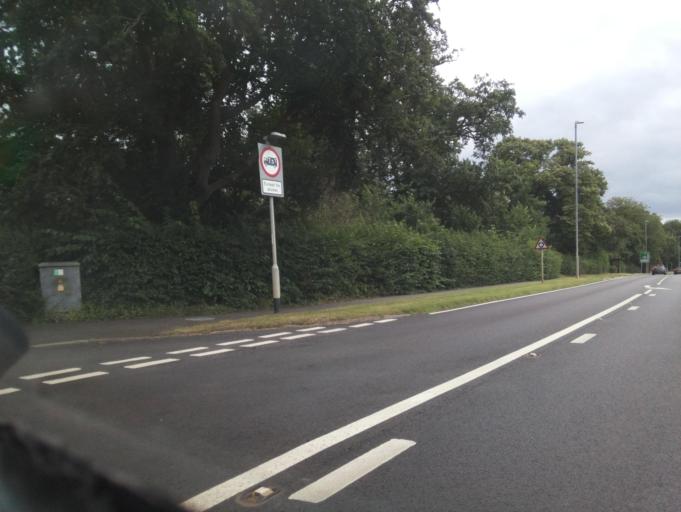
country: GB
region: England
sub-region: District of Rutland
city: Ryhall
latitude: 52.6822
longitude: -0.4737
